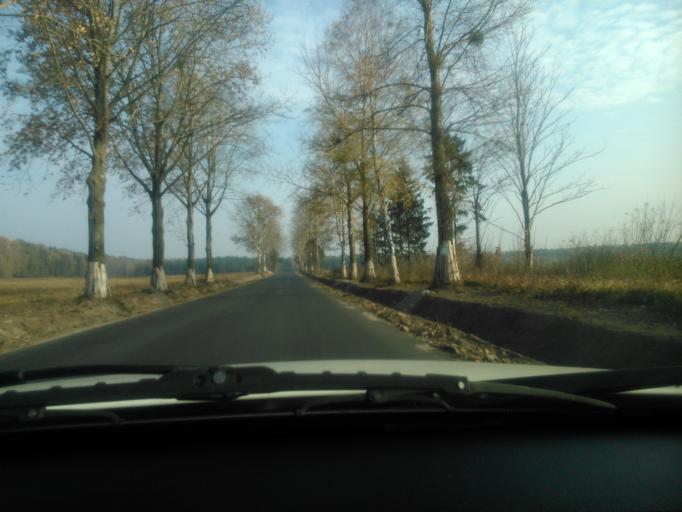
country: PL
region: Warmian-Masurian Voivodeship
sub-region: Powiat dzialdowski
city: Lidzbark
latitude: 53.2573
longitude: 19.8749
